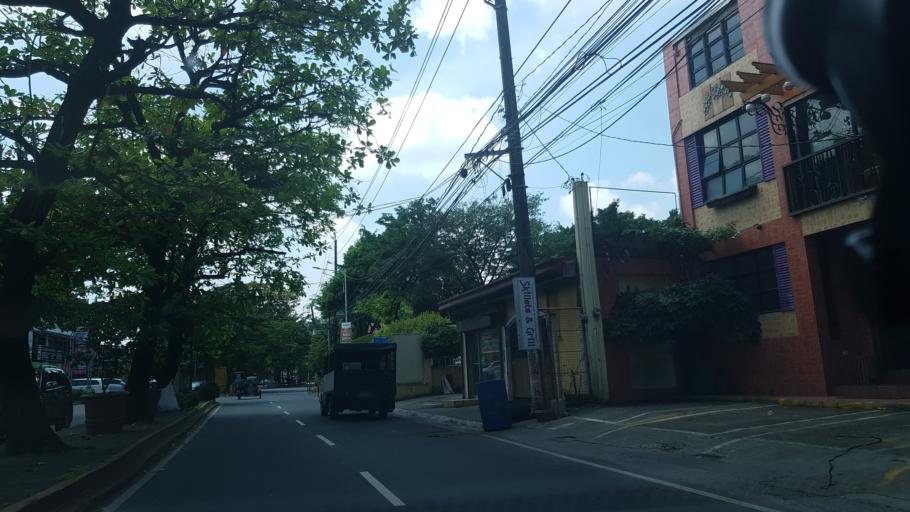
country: PH
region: Calabarzon
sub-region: Province of Rizal
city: Las Pinas
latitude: 14.4404
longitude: 120.9912
